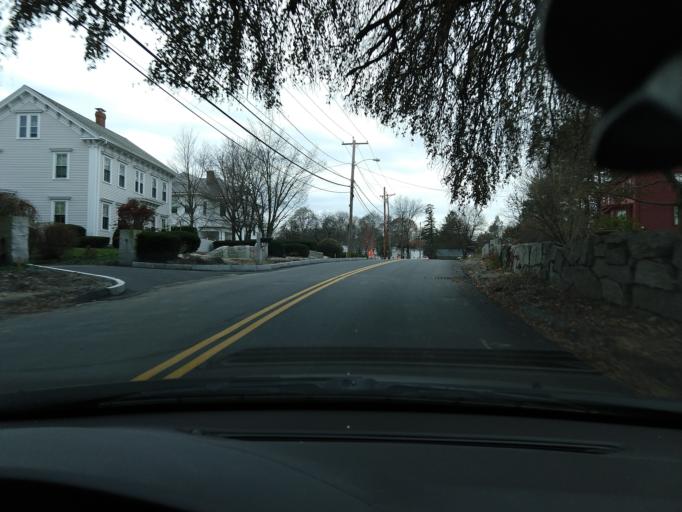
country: US
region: Massachusetts
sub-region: Middlesex County
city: Westford
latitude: 42.5838
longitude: -71.4336
